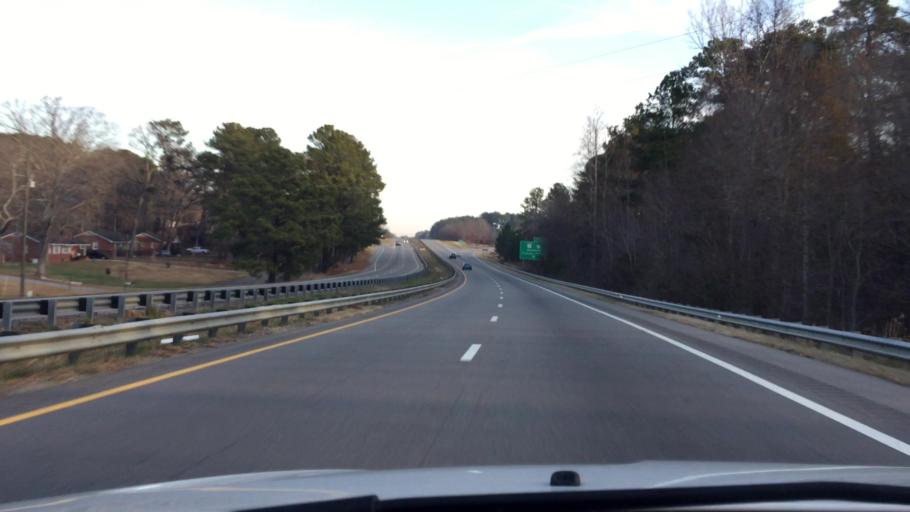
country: US
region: North Carolina
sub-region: Lee County
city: Sanford
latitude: 35.4628
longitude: -79.2051
